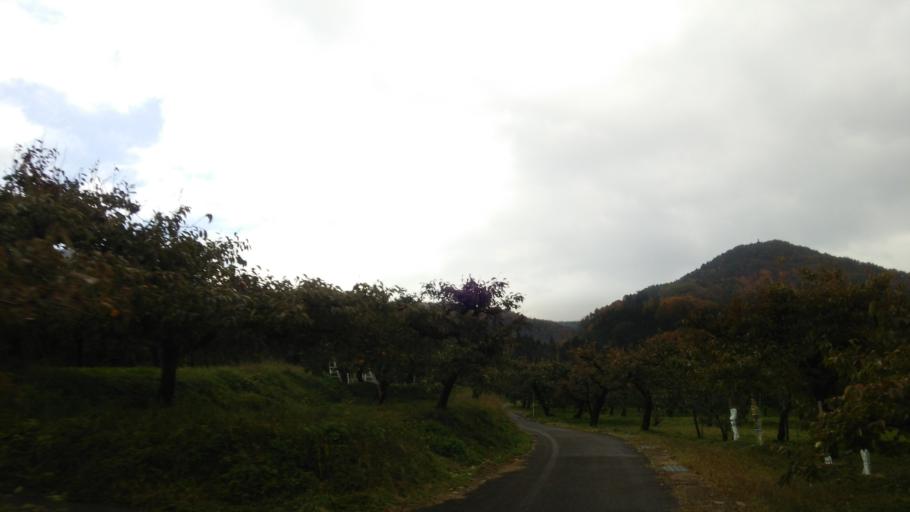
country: JP
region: Fukushima
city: Kitakata
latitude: 37.4600
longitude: 139.9358
